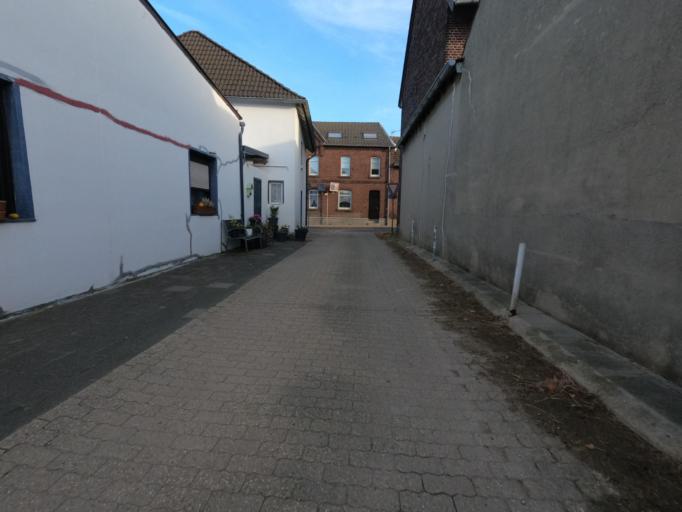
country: DE
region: North Rhine-Westphalia
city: Huckelhoven
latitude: 51.0560
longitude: 6.1995
